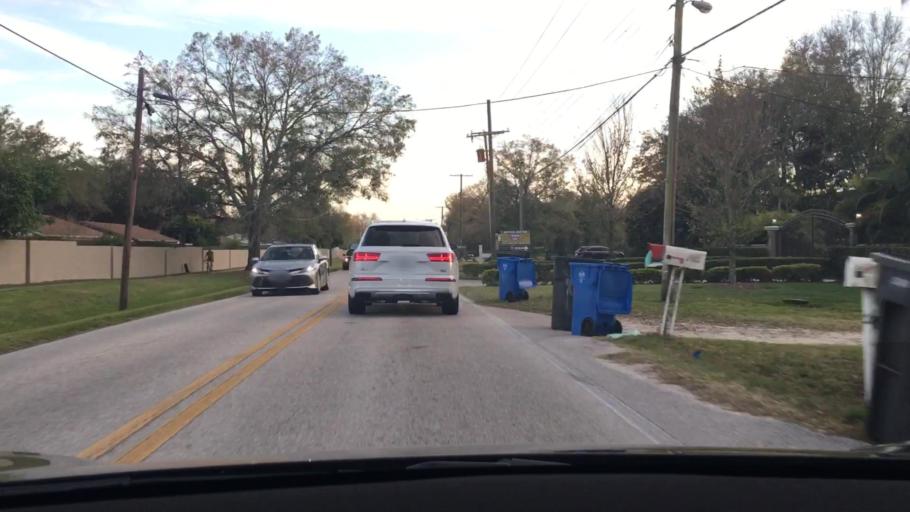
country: US
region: Florida
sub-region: Hillsborough County
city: Greater Northdale
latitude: 28.0893
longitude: -82.5399
